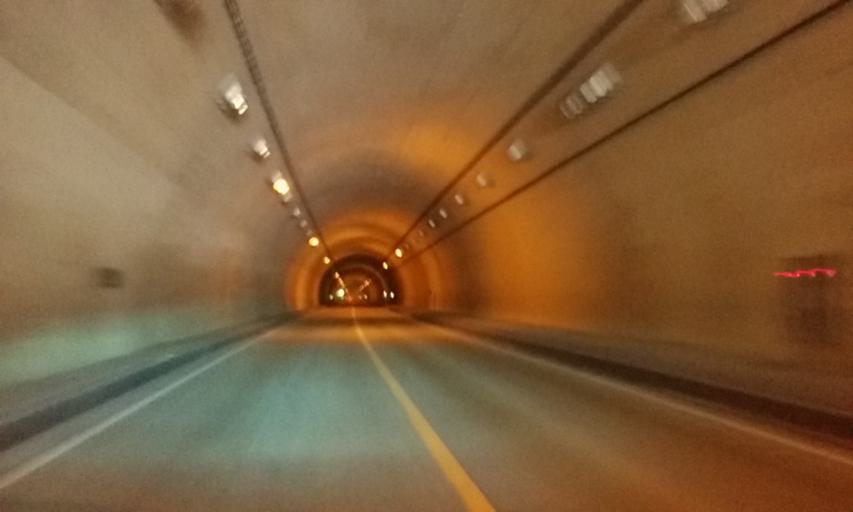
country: JP
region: Kyoto
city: Fukuchiyama
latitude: 35.4008
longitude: 135.0384
